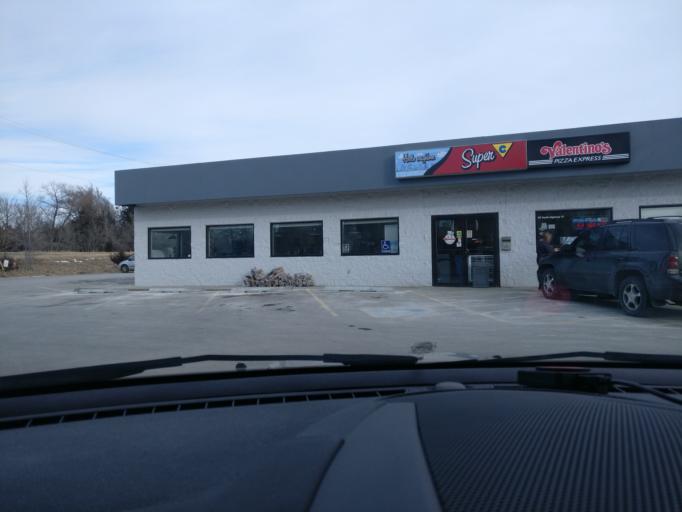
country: US
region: Nebraska
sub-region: Saunders County
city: Wahoo
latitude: 41.0531
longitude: -96.6412
